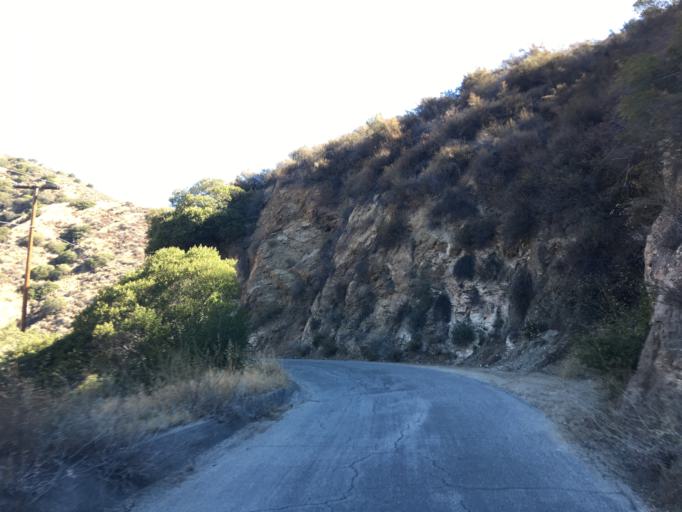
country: US
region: California
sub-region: Los Angeles County
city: La Verne
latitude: 34.1576
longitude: -117.7720
